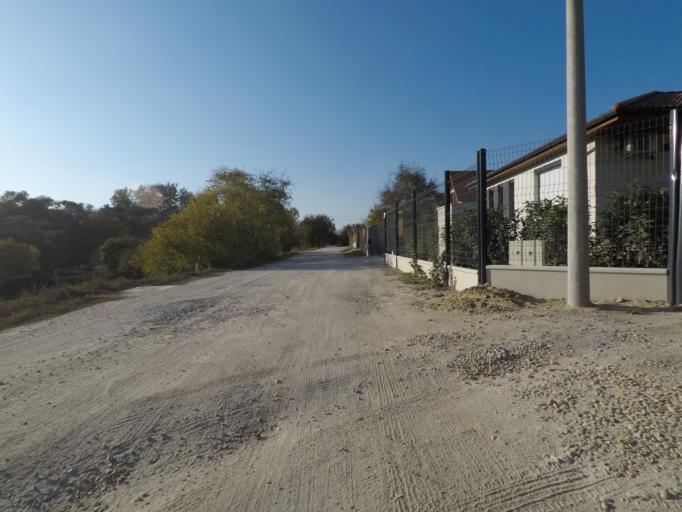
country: HU
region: Pest
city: Budakalasz
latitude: 47.6235
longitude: 19.0365
